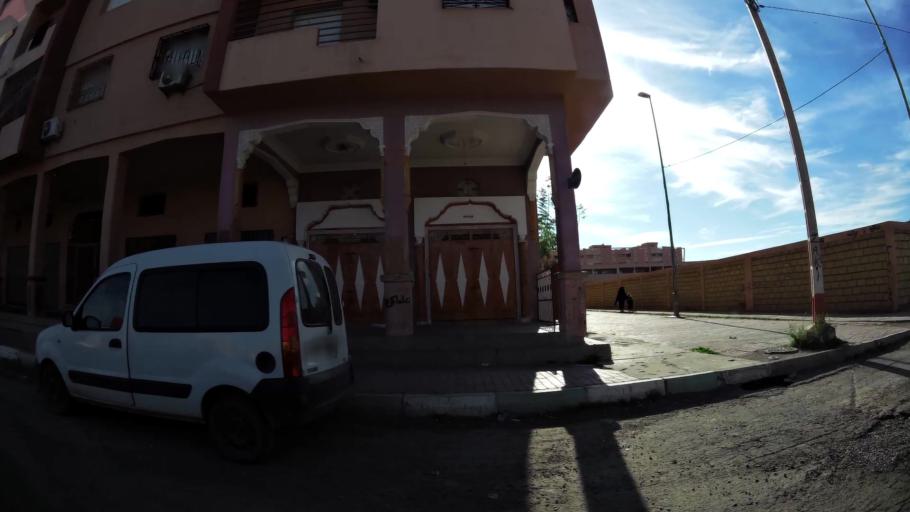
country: MA
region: Marrakech-Tensift-Al Haouz
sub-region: Marrakech
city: Marrakesh
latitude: 31.6868
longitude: -8.0625
